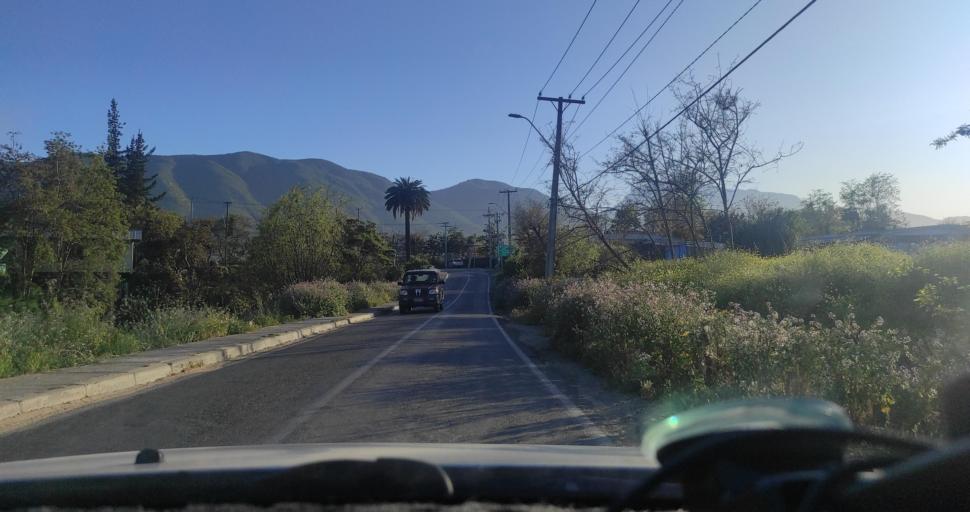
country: CL
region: Valparaiso
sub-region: Provincia de Marga Marga
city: Limache
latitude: -32.9983
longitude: -71.2213
